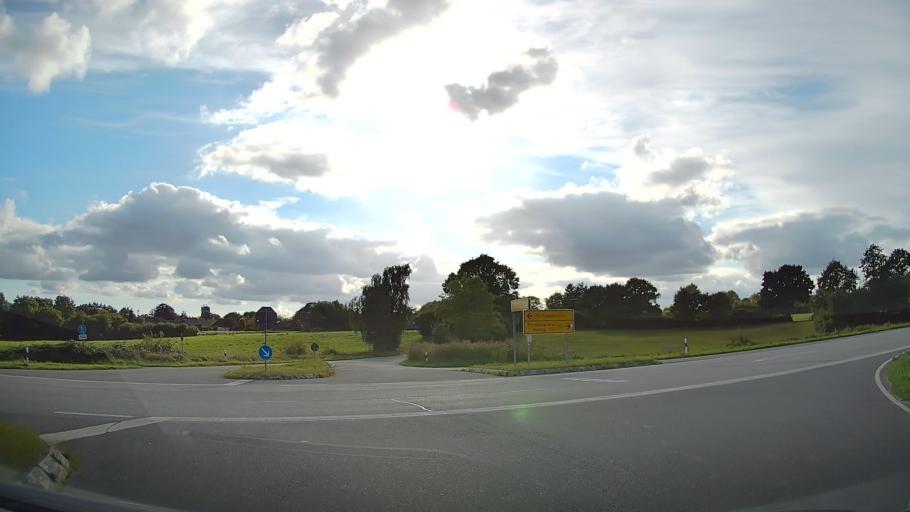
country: DE
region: Schleswig-Holstein
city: Nieby
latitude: 54.7359
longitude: 9.9374
